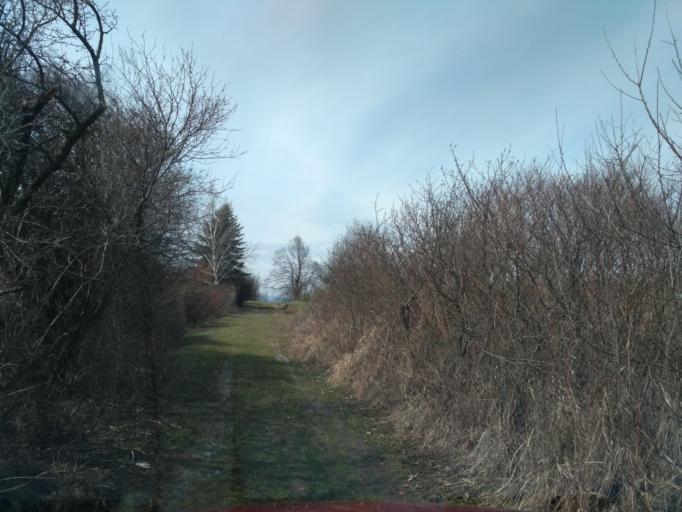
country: SK
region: Kosicky
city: Kosice
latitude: 48.7089
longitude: 21.2902
